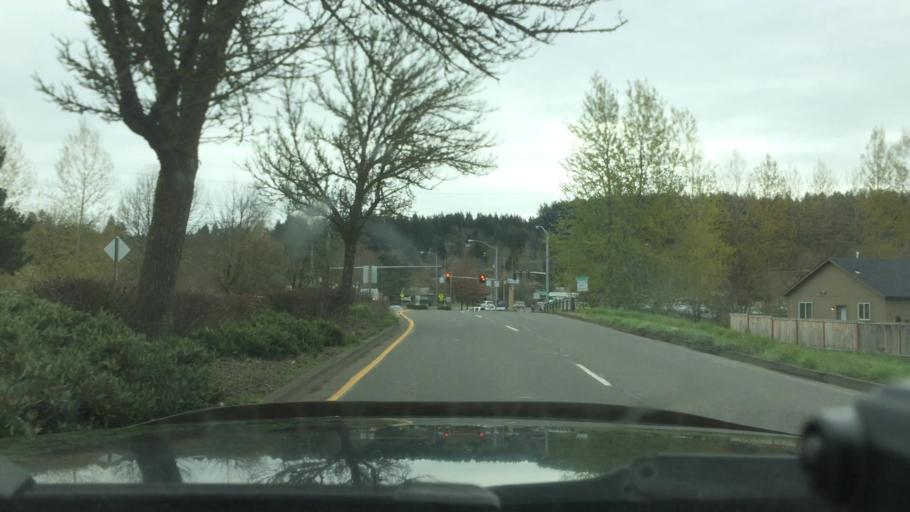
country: US
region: Oregon
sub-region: Lane County
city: Eugene
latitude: 44.0244
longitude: -123.0830
